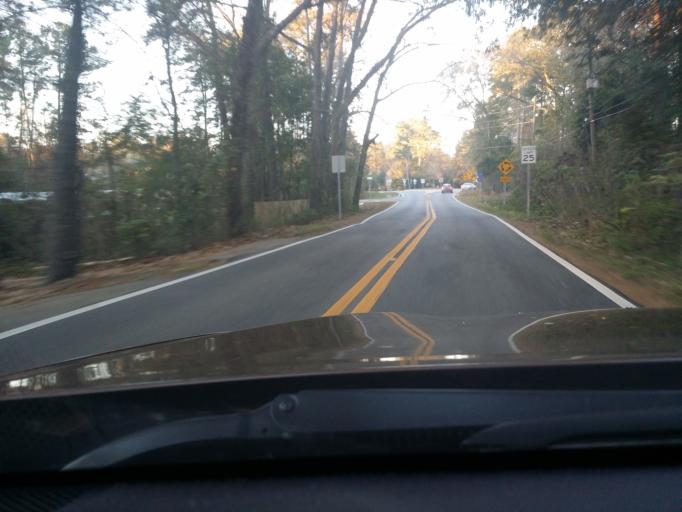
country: US
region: Florida
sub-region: Leon County
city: Tallahassee
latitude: 30.4766
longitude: -84.2181
